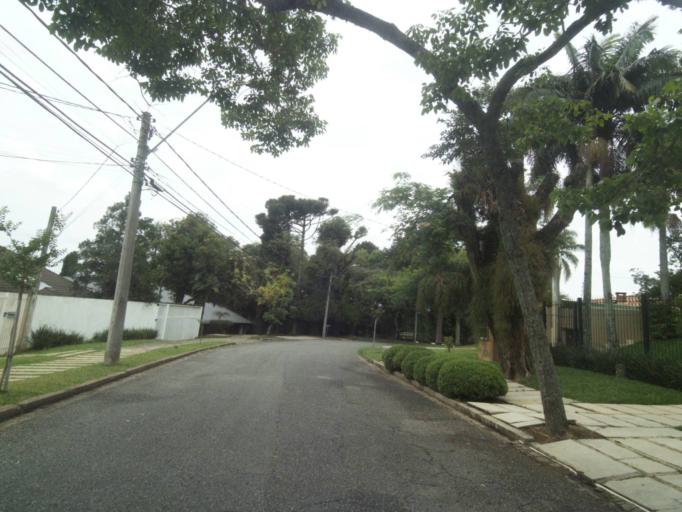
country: BR
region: Parana
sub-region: Curitiba
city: Curitiba
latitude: -25.4059
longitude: -49.2840
